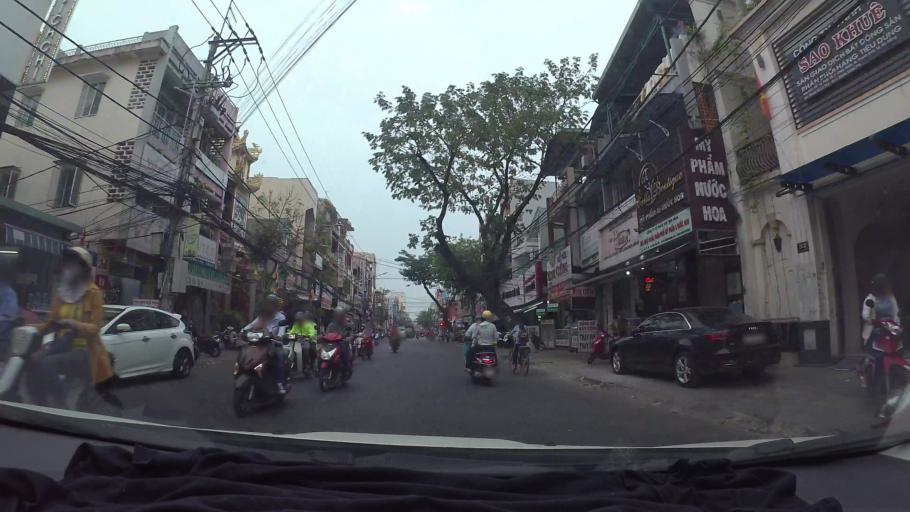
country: VN
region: Da Nang
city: Da Nang
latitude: 16.0664
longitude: 108.2094
